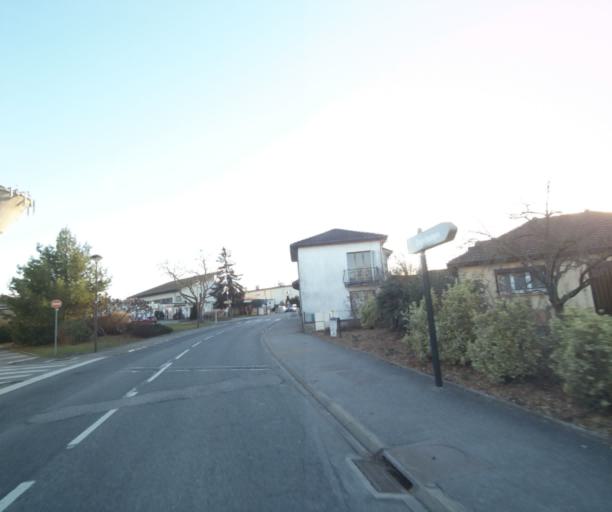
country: FR
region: Lorraine
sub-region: Departement de Meurthe-et-Moselle
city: Pulnoy
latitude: 48.7010
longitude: 6.2568
